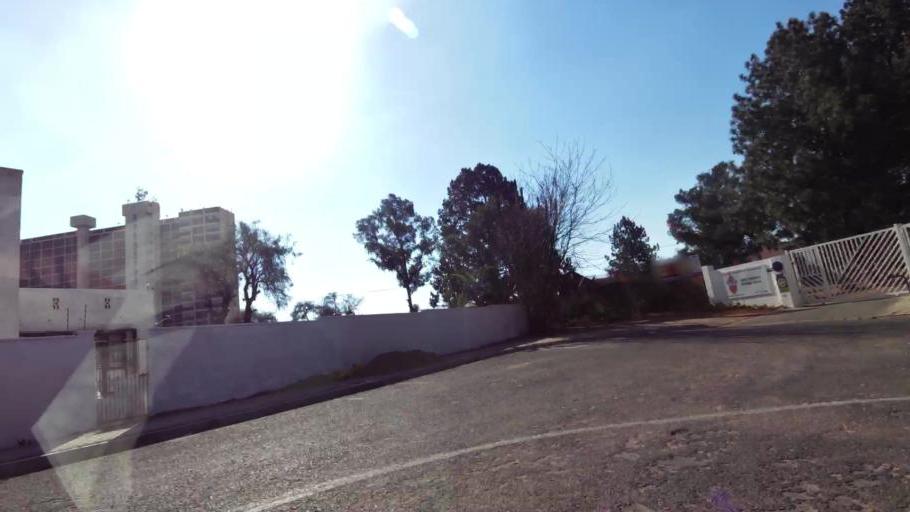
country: ZA
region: Gauteng
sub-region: City of Johannesburg Metropolitan Municipality
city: Johannesburg
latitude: -26.1714
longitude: 27.9840
